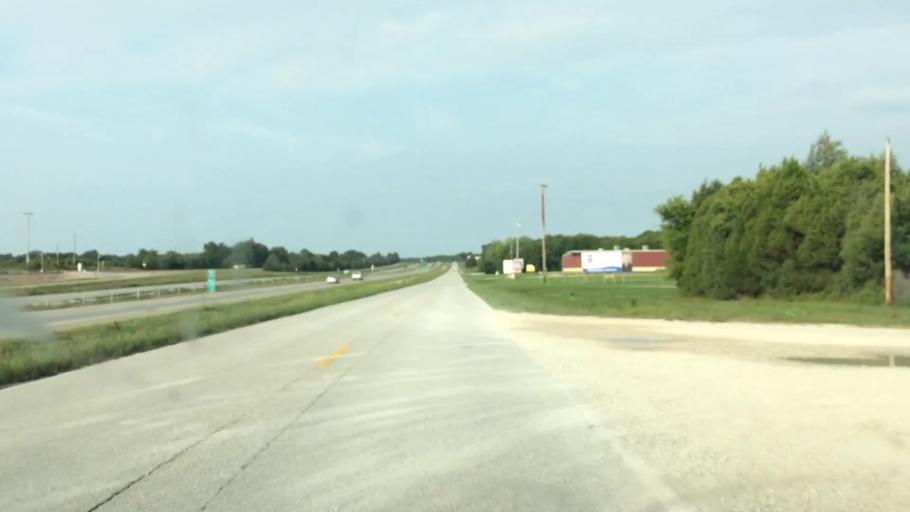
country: US
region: Missouri
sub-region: Greene County
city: Strafford
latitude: 37.2905
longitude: -93.0274
